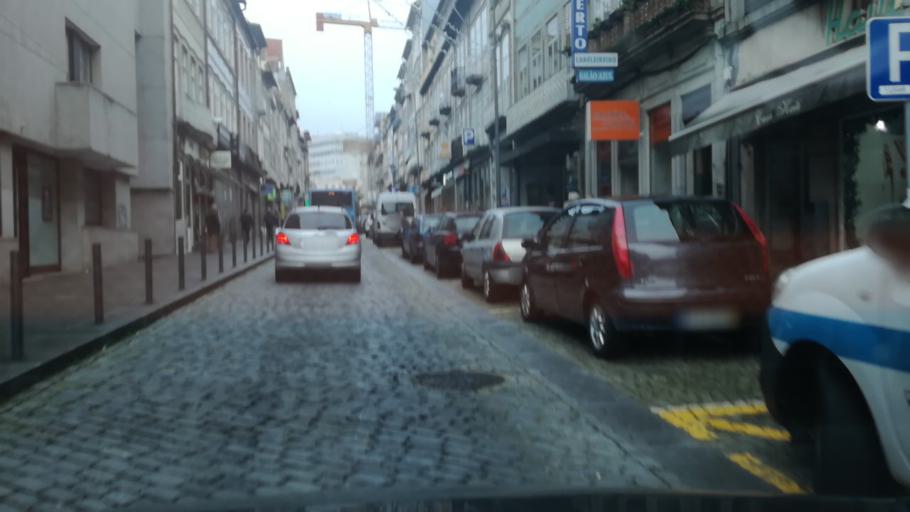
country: PT
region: Braga
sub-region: Braga
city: Braga
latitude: 41.5522
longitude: -8.4236
